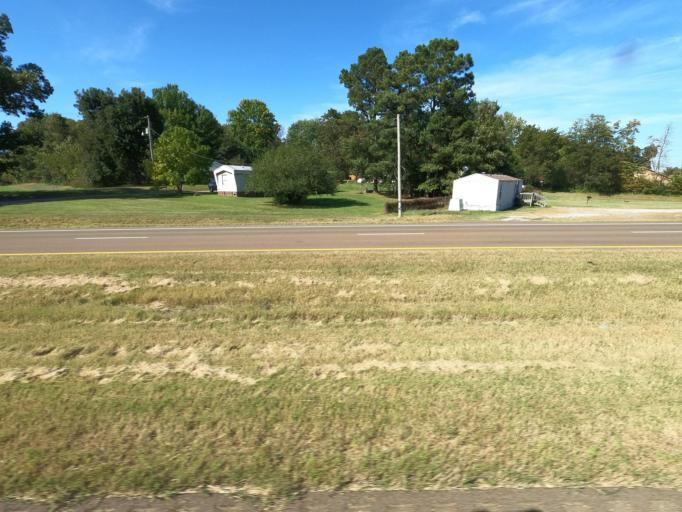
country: US
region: Tennessee
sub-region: Obion County
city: Troy
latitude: 36.3347
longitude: -89.1612
